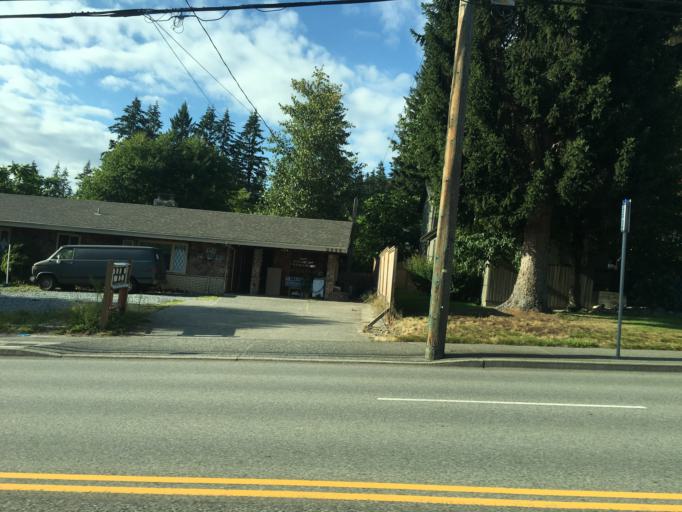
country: CA
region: British Columbia
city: Port Moody
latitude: 49.2490
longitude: -122.8286
